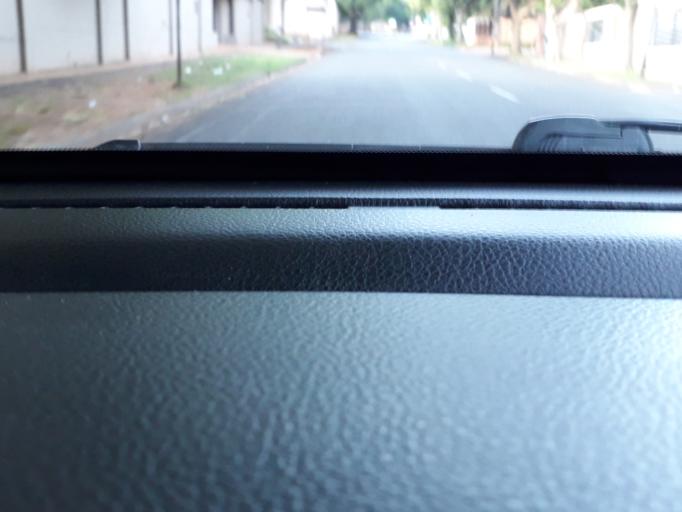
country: ZA
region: Gauteng
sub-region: City of Johannesburg Metropolitan Municipality
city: Johannesburg
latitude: -26.1668
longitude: 28.0566
